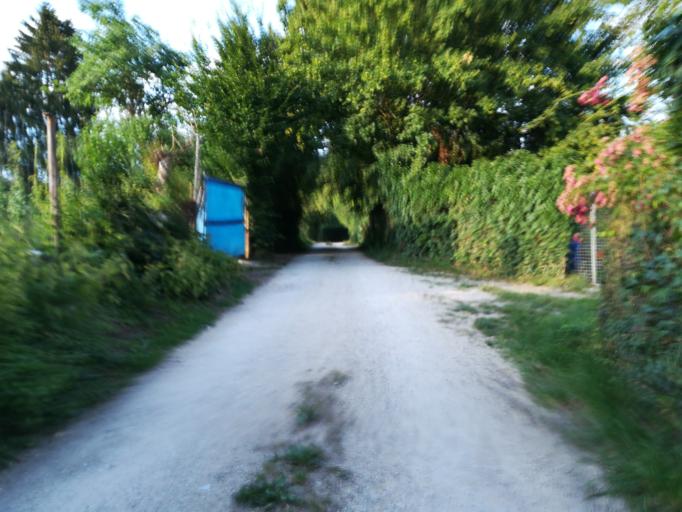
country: DE
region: Baden-Wuerttemberg
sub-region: Freiburg Region
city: Singen
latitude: 47.7544
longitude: 8.8285
